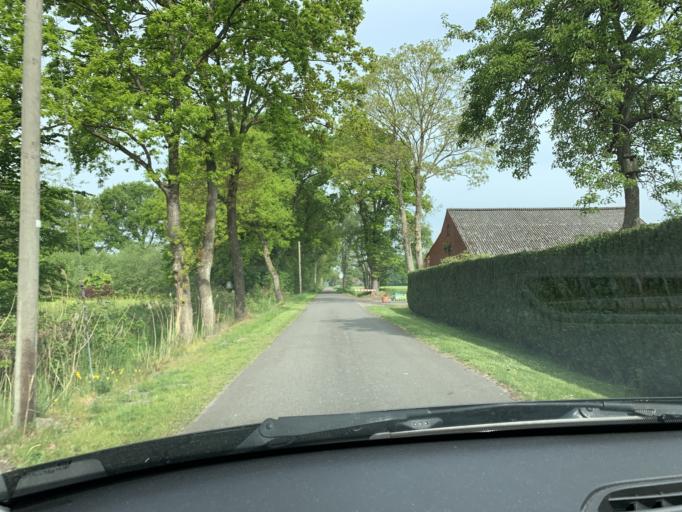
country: DE
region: Lower Saxony
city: Apen
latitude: 53.2337
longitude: 7.8383
